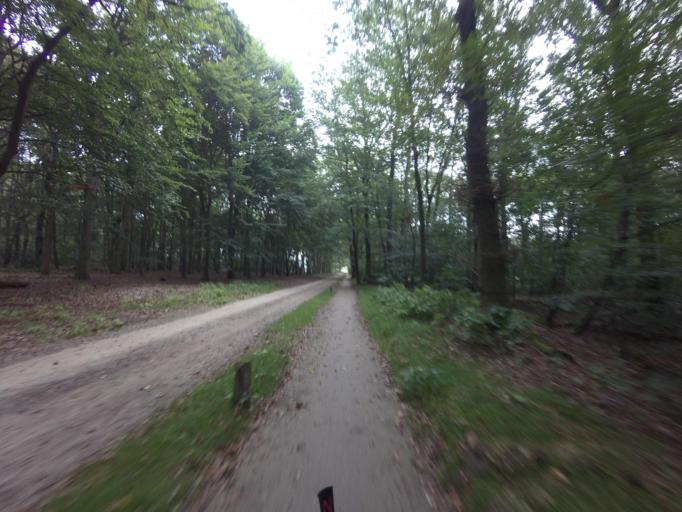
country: DE
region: Lower Saxony
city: Getelo
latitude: 52.4351
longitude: 6.8858
